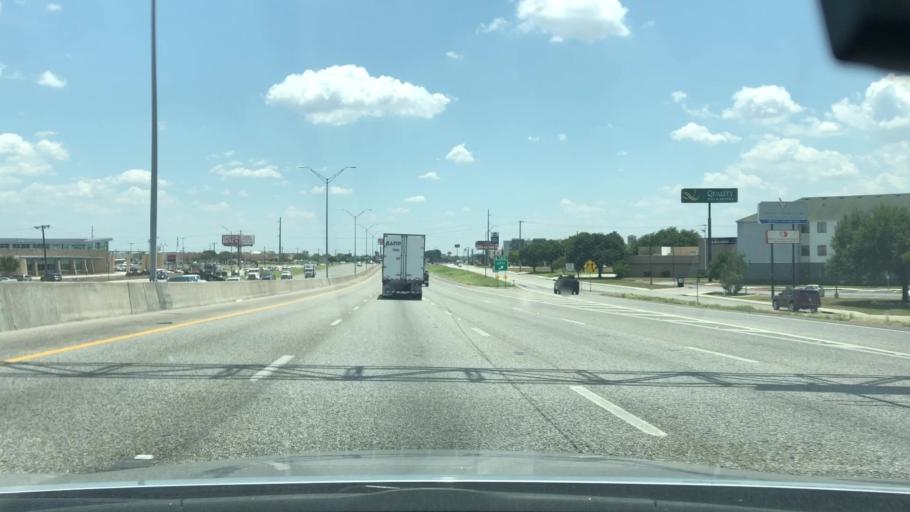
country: US
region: Texas
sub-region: Comal County
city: New Braunfels
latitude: 29.7113
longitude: -98.0902
